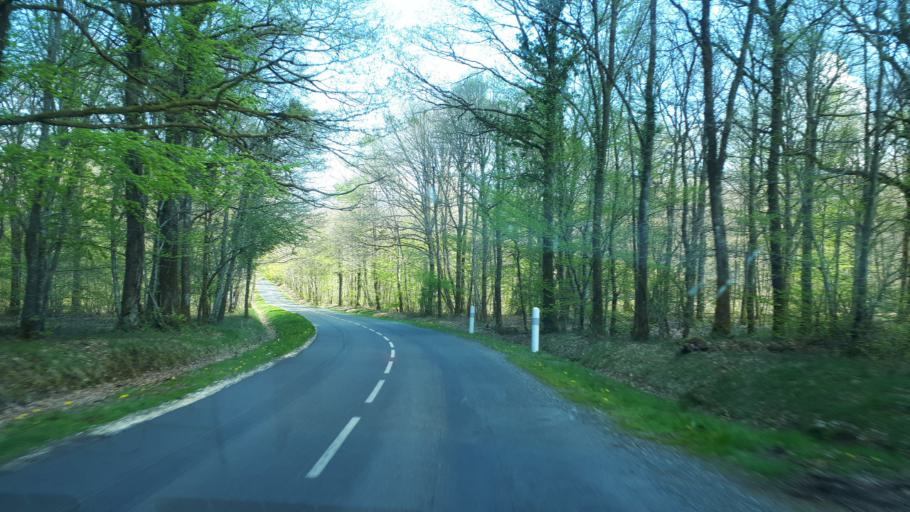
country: FR
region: Centre
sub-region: Departement du Cher
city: Henrichemont
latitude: 47.2990
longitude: 2.6169
